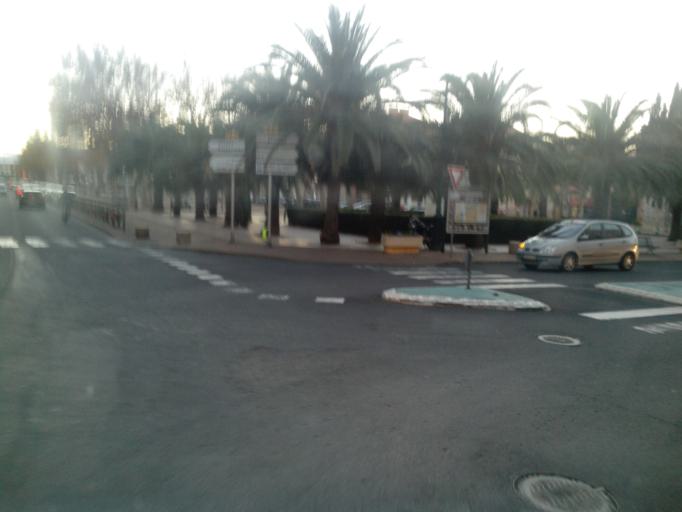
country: FR
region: Languedoc-Roussillon
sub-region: Departement des Pyrenees-Orientales
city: Rivesaltes
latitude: 42.7686
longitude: 2.8718
